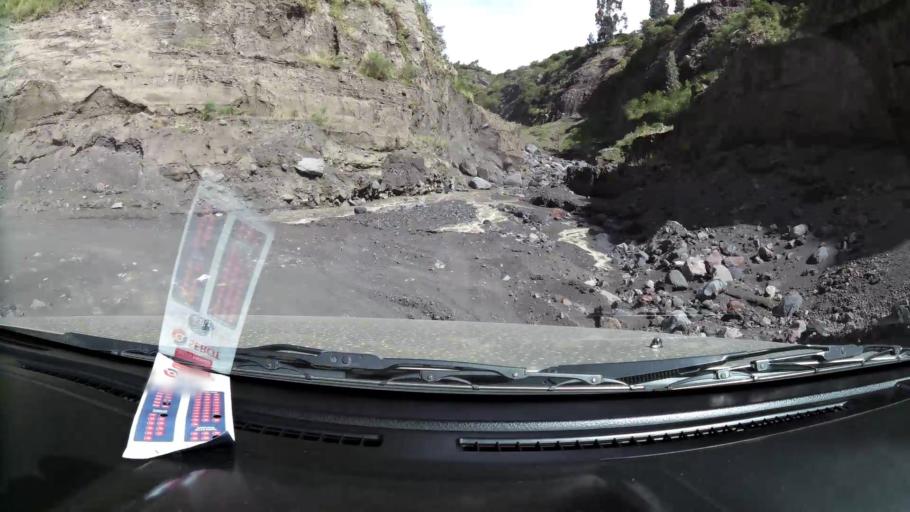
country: EC
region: Tungurahua
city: Banos
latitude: -1.4794
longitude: -78.5125
